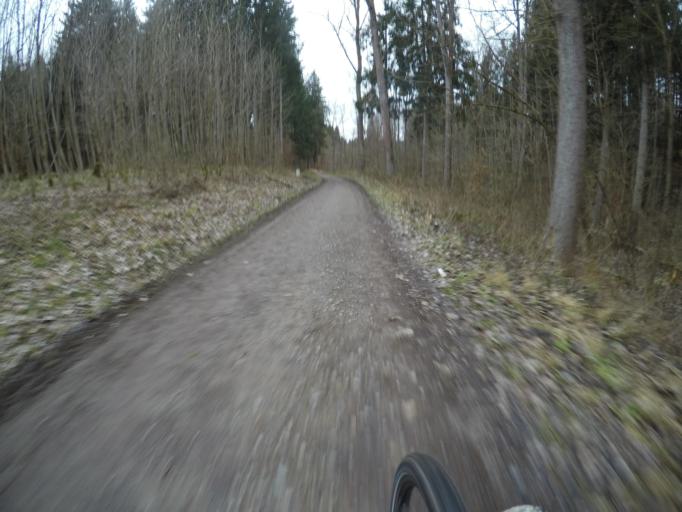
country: DE
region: Baden-Wuerttemberg
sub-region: Regierungsbezirk Stuttgart
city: Sindelfingen
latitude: 48.6957
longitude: 9.0528
